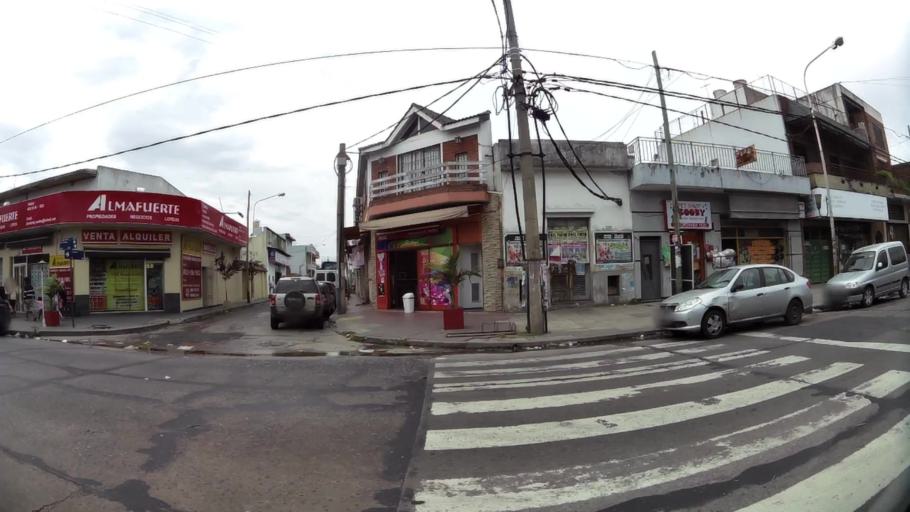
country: AR
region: Buenos Aires F.D.
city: Villa Lugano
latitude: -34.6826
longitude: -58.5150
